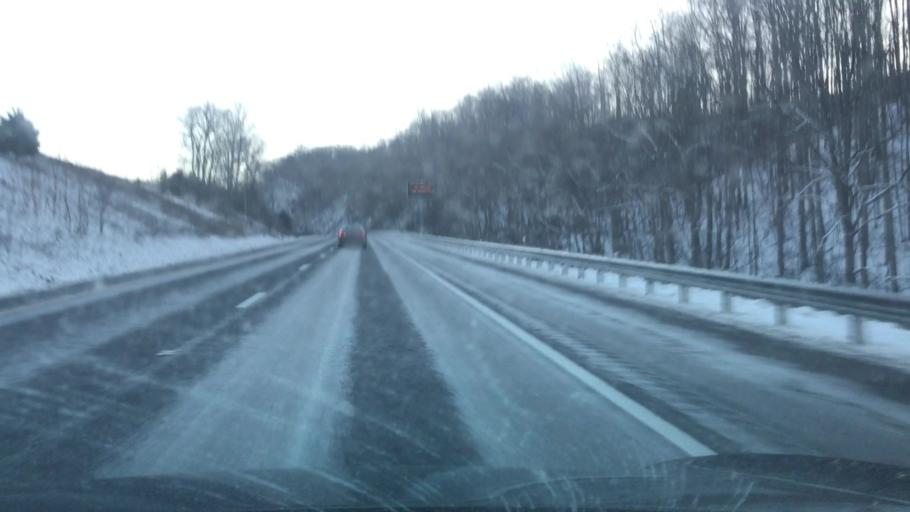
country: US
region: Virginia
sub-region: Montgomery County
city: Shawsville
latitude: 37.1843
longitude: -80.2876
